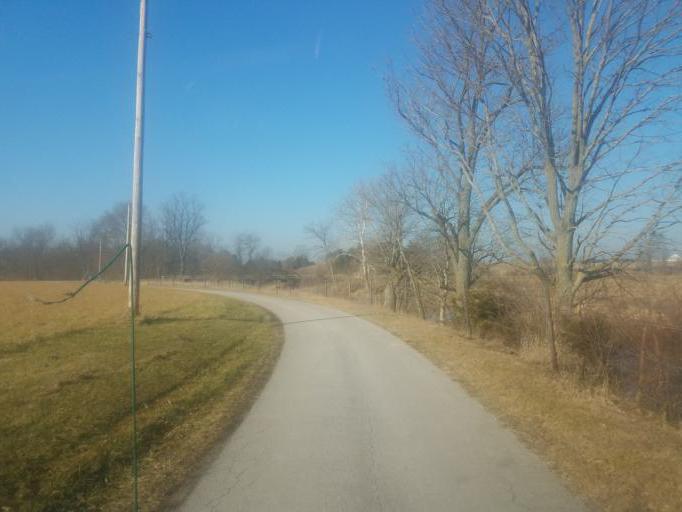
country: US
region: Ohio
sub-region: Seneca County
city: Tiffin
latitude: 41.0607
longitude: -83.0329
